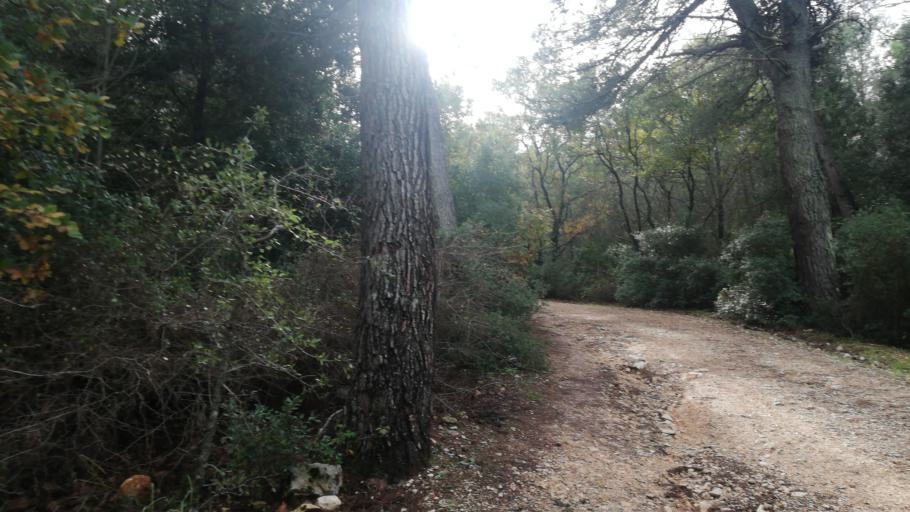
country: IT
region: Apulia
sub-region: Provincia di Bari
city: Cassano delle Murge
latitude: 40.8805
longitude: 16.7106
